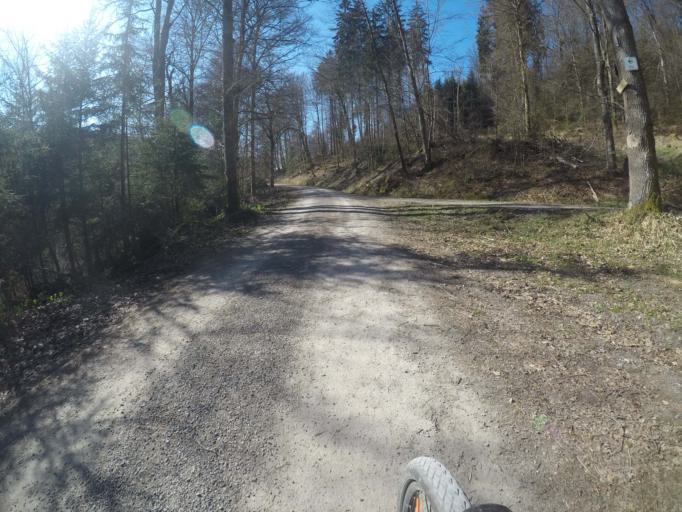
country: DE
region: Baden-Wuerttemberg
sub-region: Tuebingen Region
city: Tuebingen
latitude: 48.5750
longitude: 9.0331
